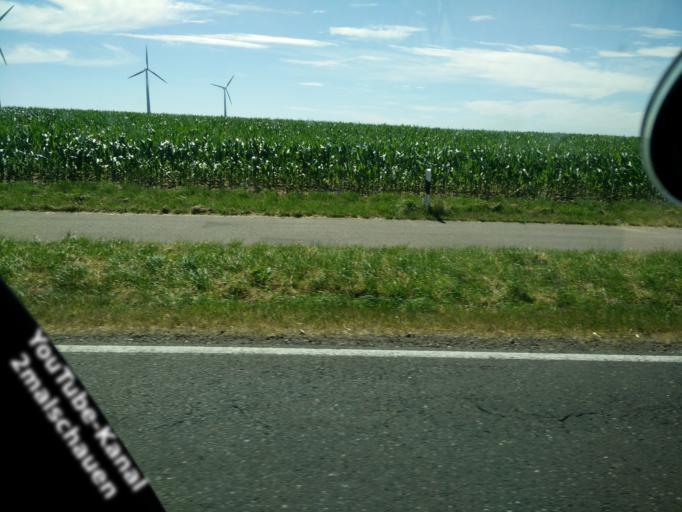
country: DE
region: Saxony
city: Waldheim
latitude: 51.0902
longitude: 13.0446
